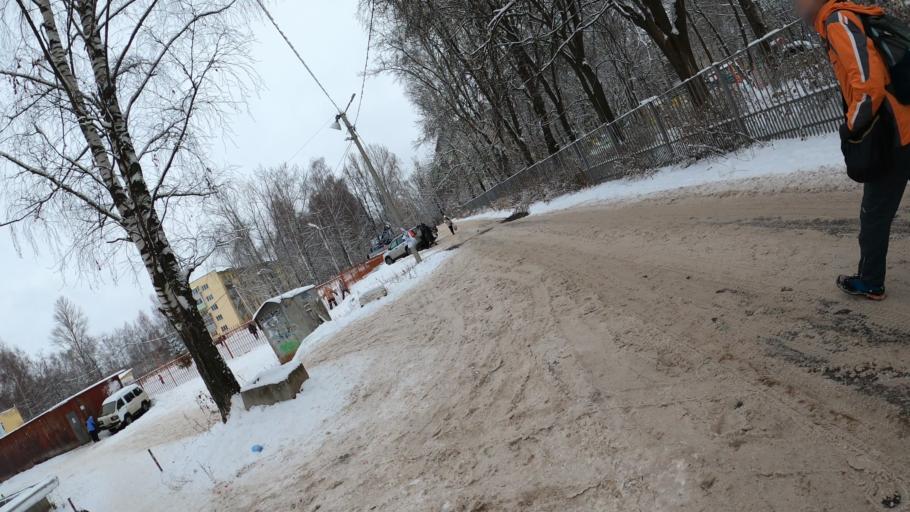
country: RU
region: Jaroslavl
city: Pereslavl'-Zalesskiy
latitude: 56.7527
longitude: 38.8714
